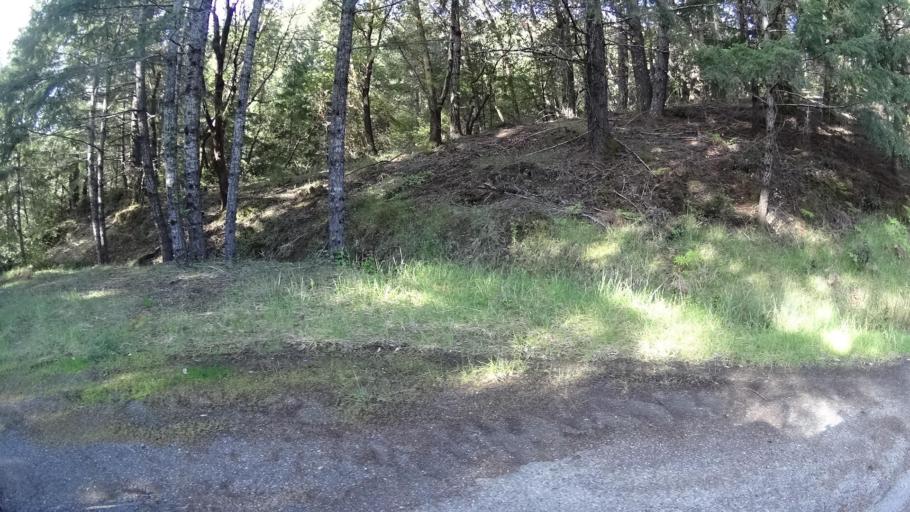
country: US
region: California
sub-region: Humboldt County
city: Rio Dell
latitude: 40.3257
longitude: -124.0467
